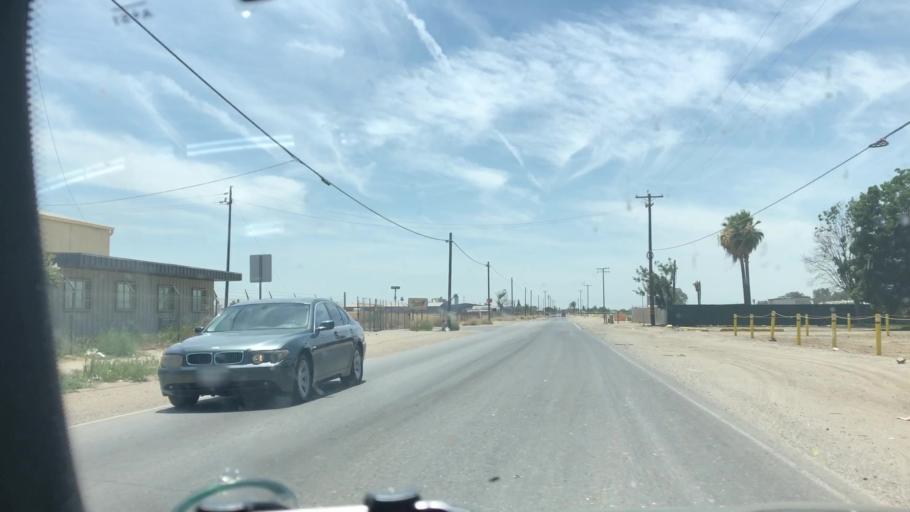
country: US
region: California
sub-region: Fresno County
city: Easton
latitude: 36.6860
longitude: -119.7546
